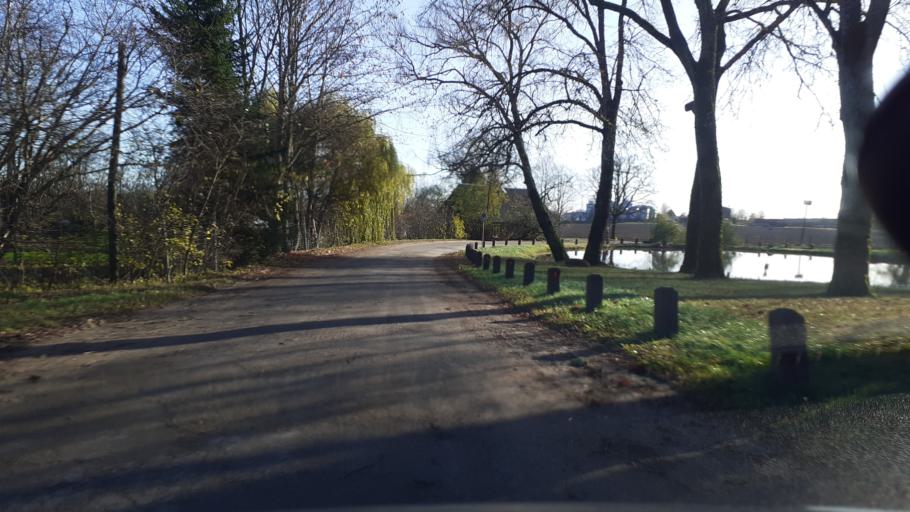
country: LV
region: Kuldigas Rajons
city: Kuldiga
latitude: 57.0005
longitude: 21.8877
